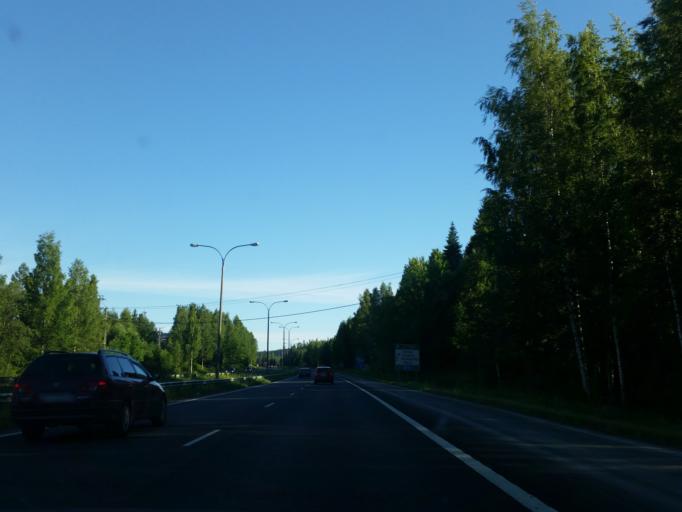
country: FI
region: Northern Savo
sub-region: Kuopio
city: Kuopio
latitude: 62.8724
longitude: 27.6204
